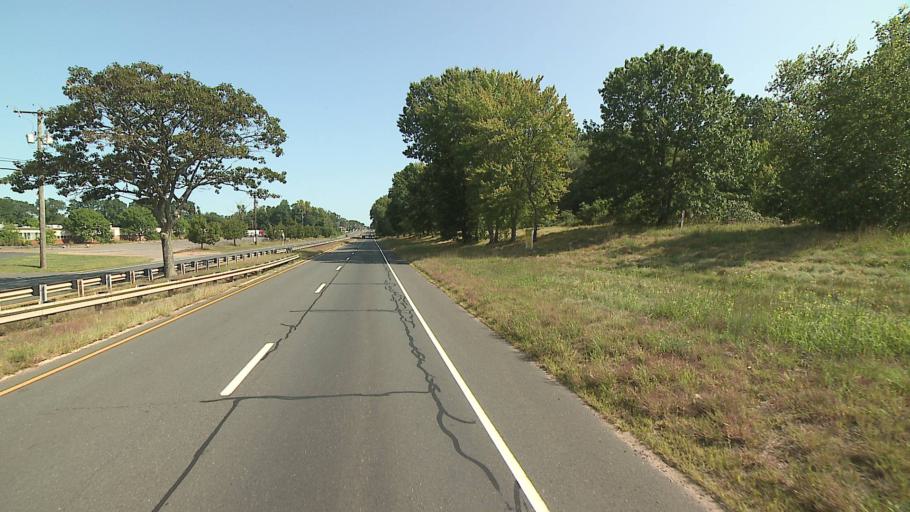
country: US
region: Connecticut
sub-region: Hartford County
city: South Windsor
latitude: 41.8134
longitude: -72.6115
